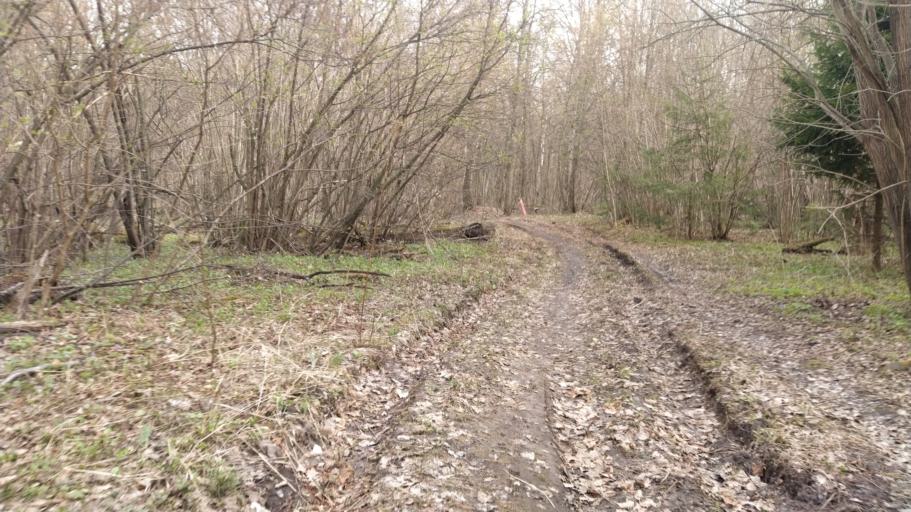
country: RU
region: Chuvashia
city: Novyye Lapsary
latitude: 56.1318
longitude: 47.1224
